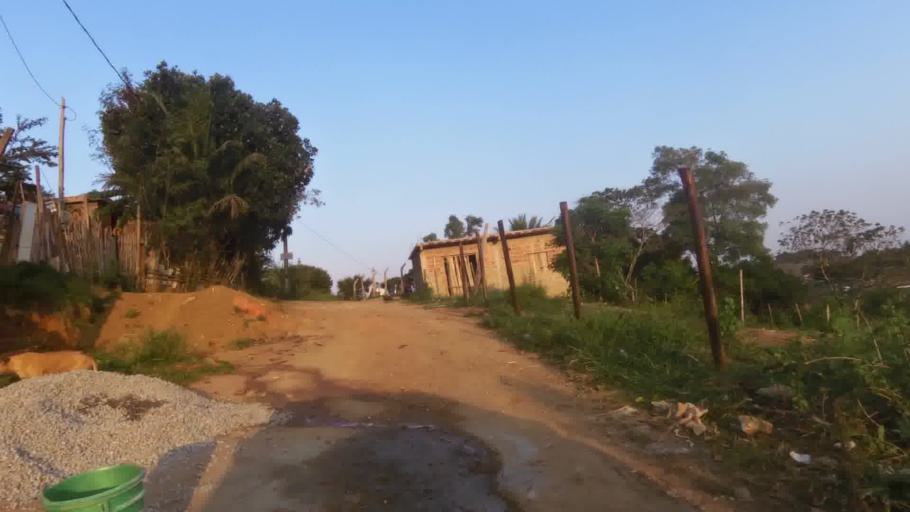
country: BR
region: Espirito Santo
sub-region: Piuma
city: Piuma
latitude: -20.8280
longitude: -40.7209
